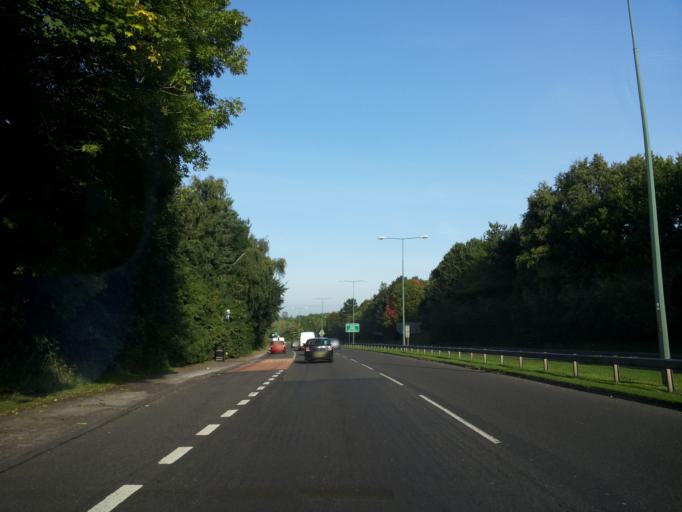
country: GB
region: England
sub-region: Solihull
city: Knowle
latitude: 52.4063
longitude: -1.7510
